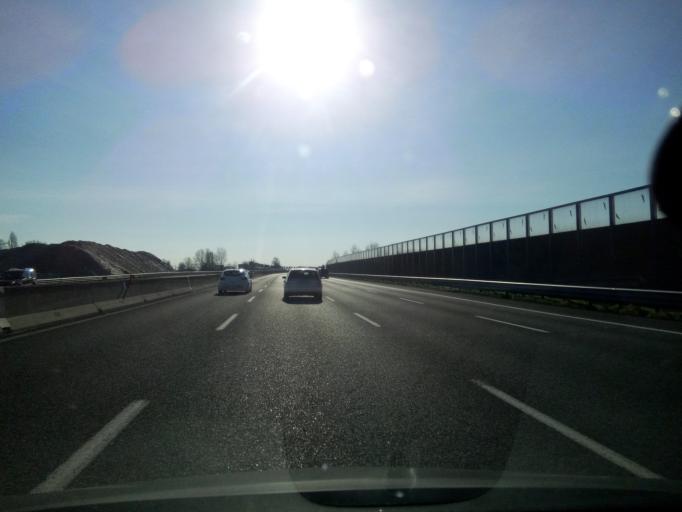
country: IT
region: Emilia-Romagna
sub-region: Provincia di Modena
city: San Cesario sul Panaro
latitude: 44.5658
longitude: 11.0393
